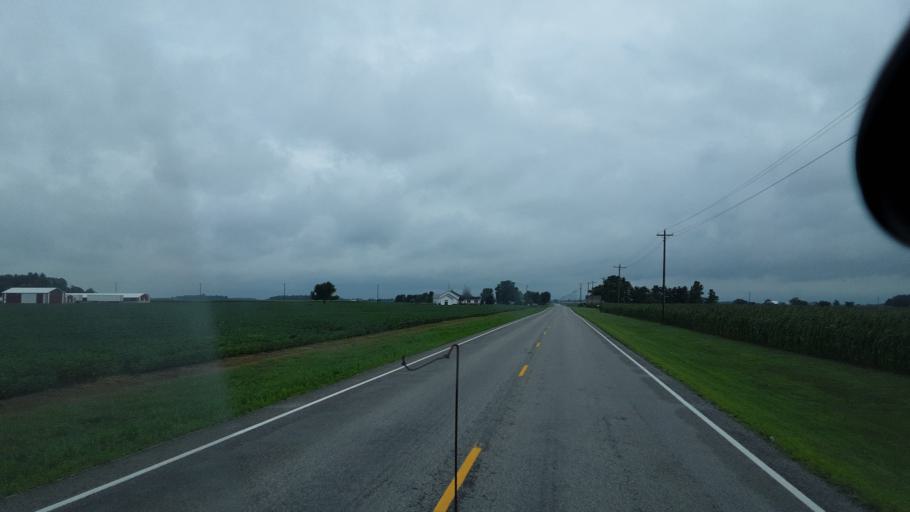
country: US
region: Indiana
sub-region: Allen County
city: Monroeville
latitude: 40.9317
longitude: -84.8620
